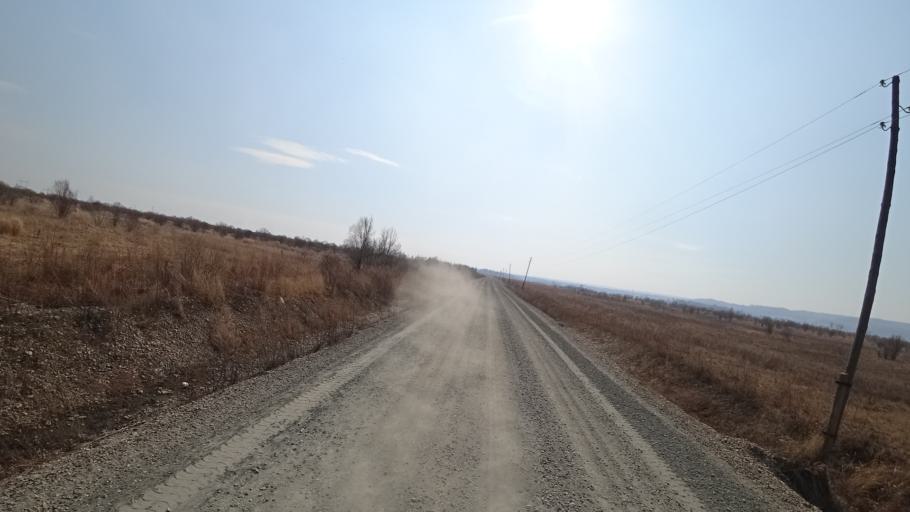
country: RU
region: Amur
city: Novobureyskiy
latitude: 49.8134
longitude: 129.9729
